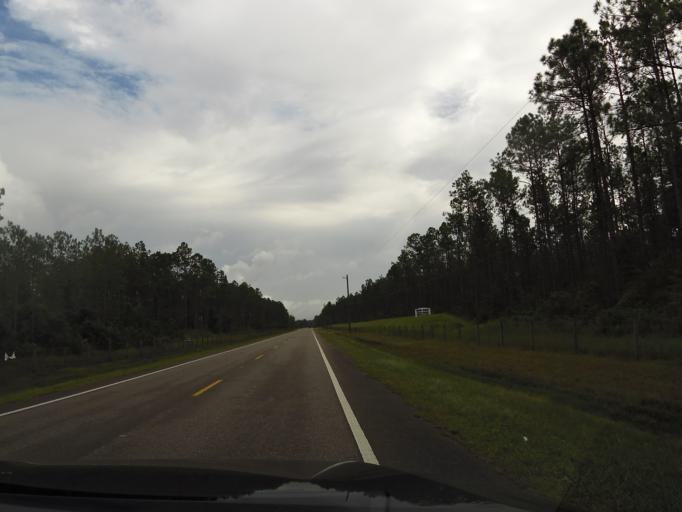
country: US
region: Florida
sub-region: Duval County
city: Baldwin
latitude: 30.3516
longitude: -81.9127
